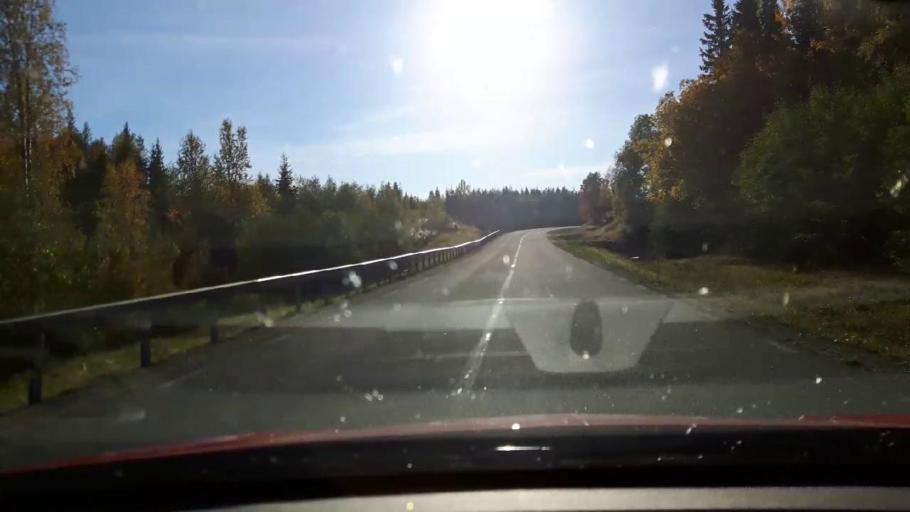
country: SE
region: Jaemtland
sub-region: Stroemsunds Kommun
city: Stroemsund
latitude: 63.8652
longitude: 15.0920
